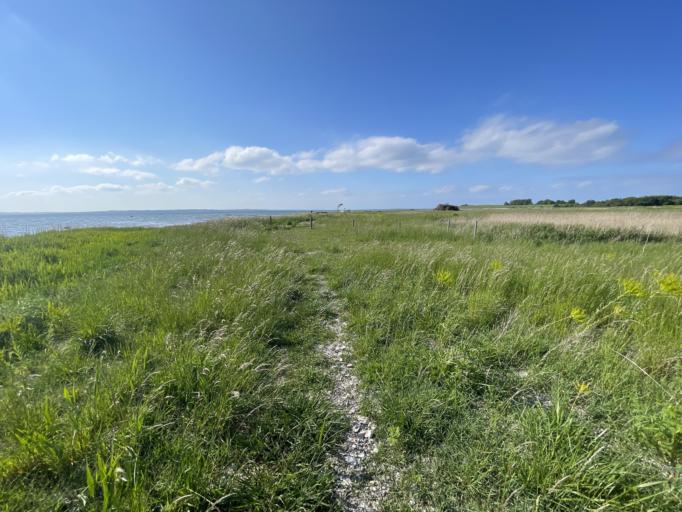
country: DK
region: Zealand
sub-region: Lejre Kommune
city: Ejby
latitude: 55.7953
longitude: 11.8249
